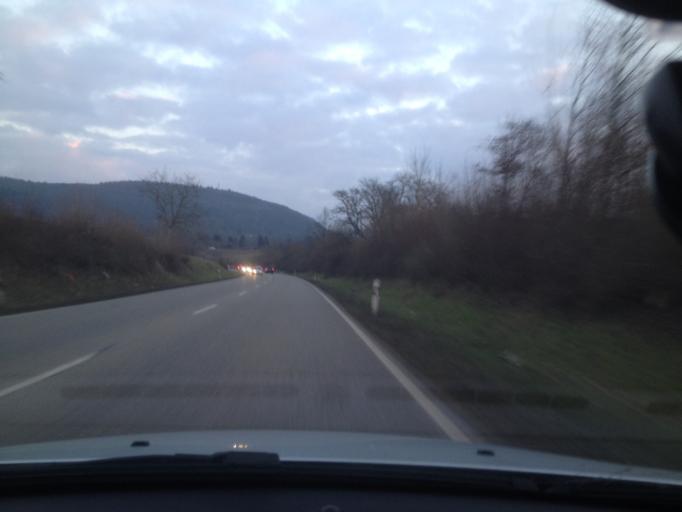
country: DE
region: Baden-Wuerttemberg
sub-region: Karlsruhe Region
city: Ettlingen
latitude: 48.9568
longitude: 8.4103
